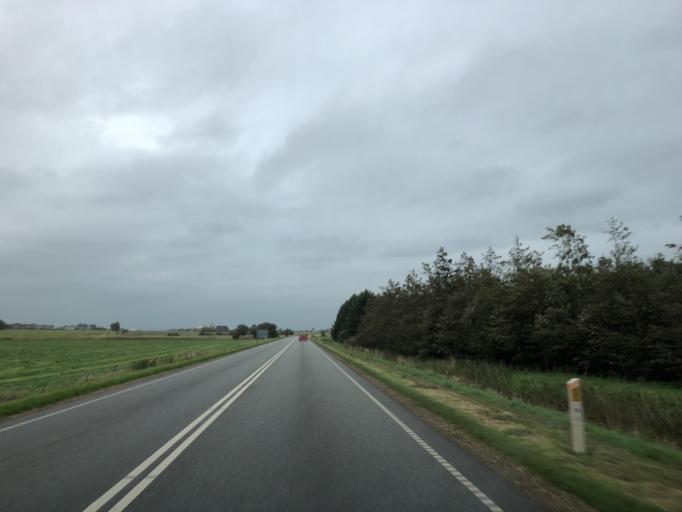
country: DK
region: Central Jutland
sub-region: Herning Kommune
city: Vildbjerg
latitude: 56.2213
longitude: 8.7359
